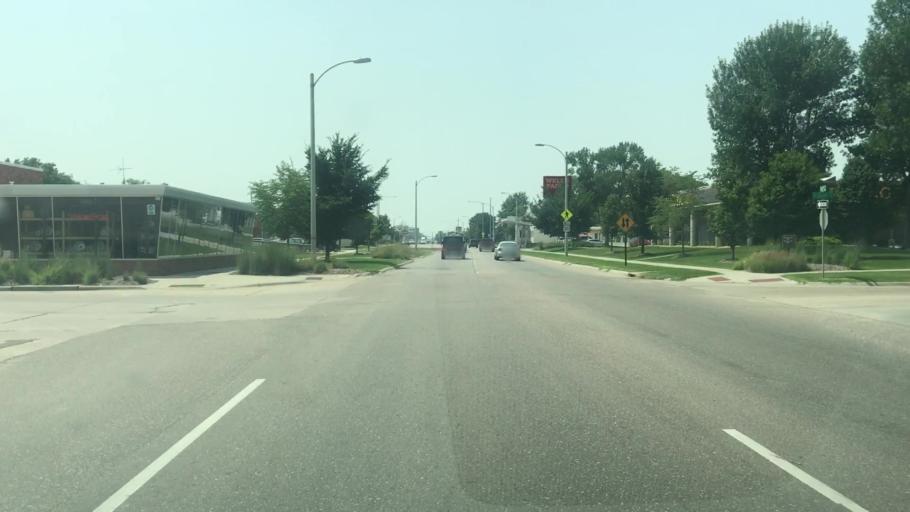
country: US
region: Nebraska
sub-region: Hall County
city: Grand Island
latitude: 40.9215
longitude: -98.3480
